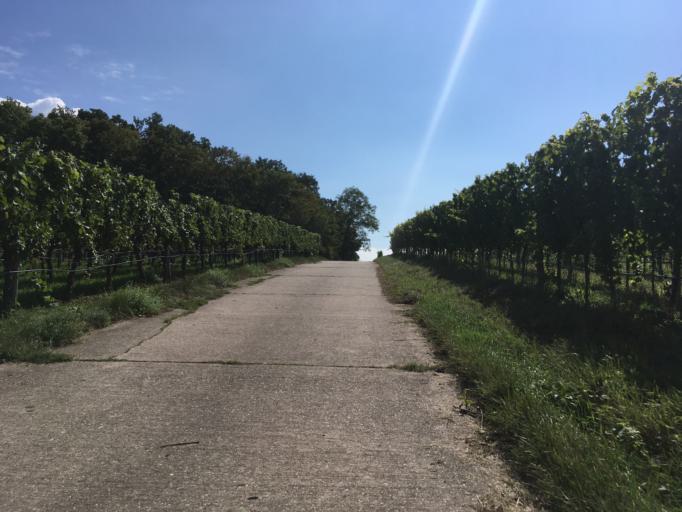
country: DE
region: Baden-Wuerttemberg
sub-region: Regierungsbezirk Stuttgart
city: Brackenheim
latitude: 49.1010
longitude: 9.0875
